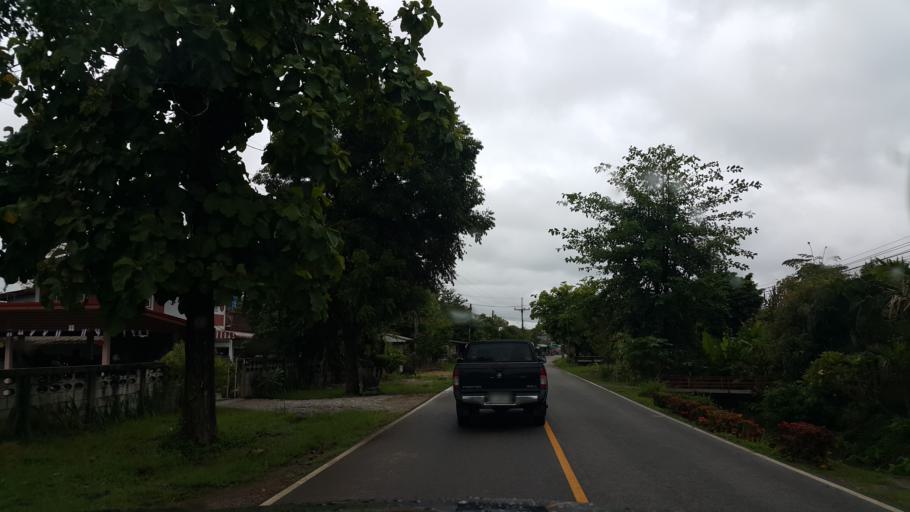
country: TH
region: Phayao
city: Chiang Kham
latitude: 19.5231
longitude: 100.3511
